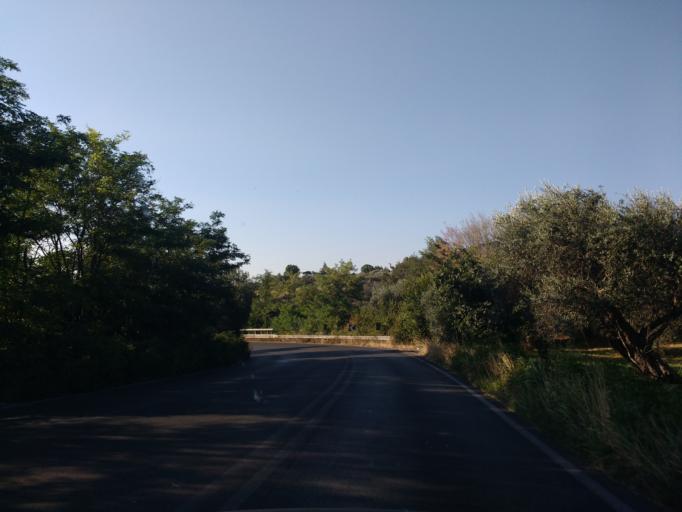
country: IT
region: Latium
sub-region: Citta metropolitana di Roma Capitale
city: Villa Adriana
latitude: 41.9537
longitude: 12.7872
